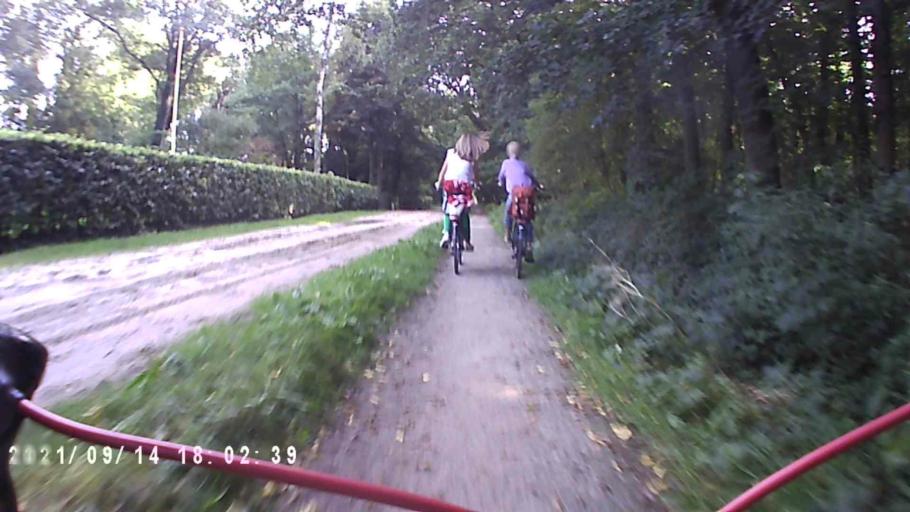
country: NL
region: Drenthe
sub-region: Gemeente Tynaarlo
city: Zuidlaren
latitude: 53.1156
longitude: 6.6518
